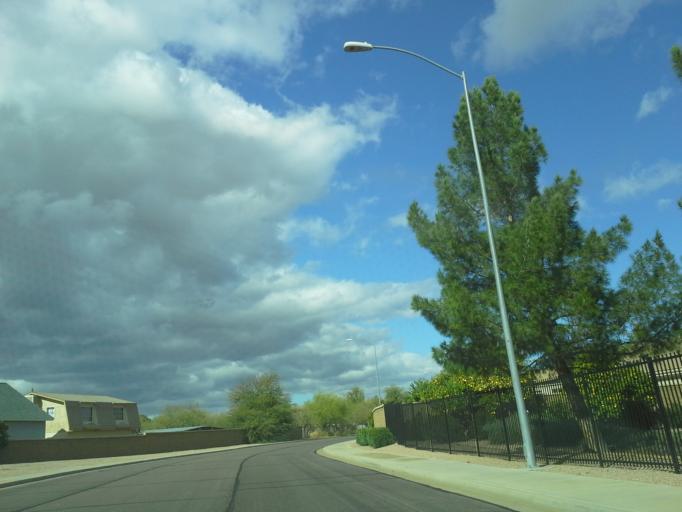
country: US
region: Arizona
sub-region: Maricopa County
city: Mesa
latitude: 33.4483
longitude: -111.7618
